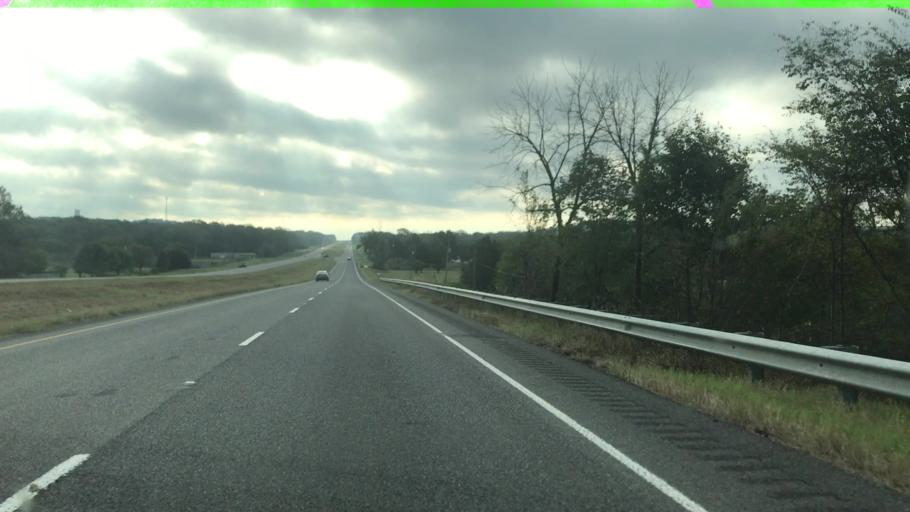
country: US
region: Alabama
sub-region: Morgan County
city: Danville
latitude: 34.4128
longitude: -87.1547
